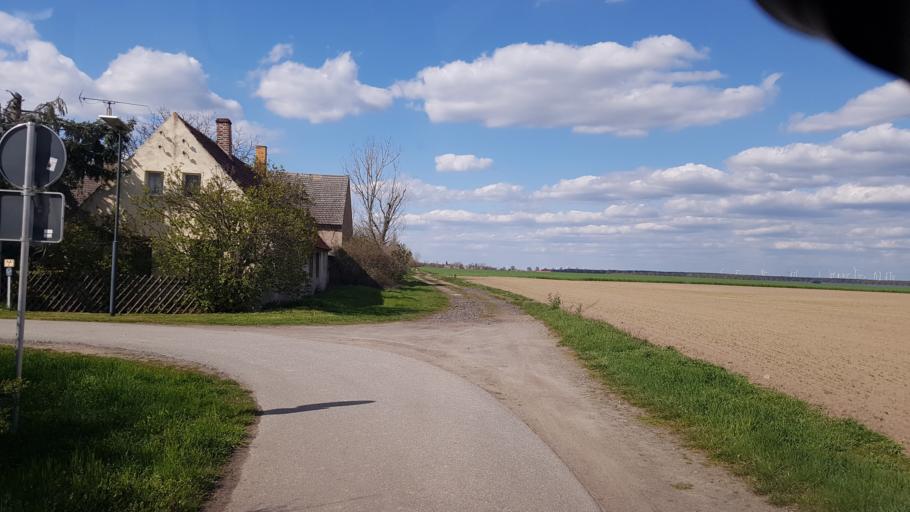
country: DE
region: Brandenburg
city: Muhlberg
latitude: 51.4572
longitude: 13.2685
